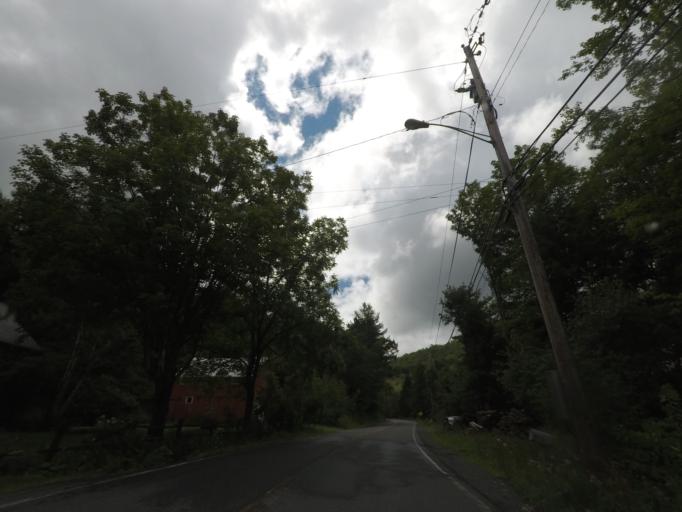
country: US
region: New York
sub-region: Rensselaer County
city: Averill Park
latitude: 42.6866
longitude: -73.3821
